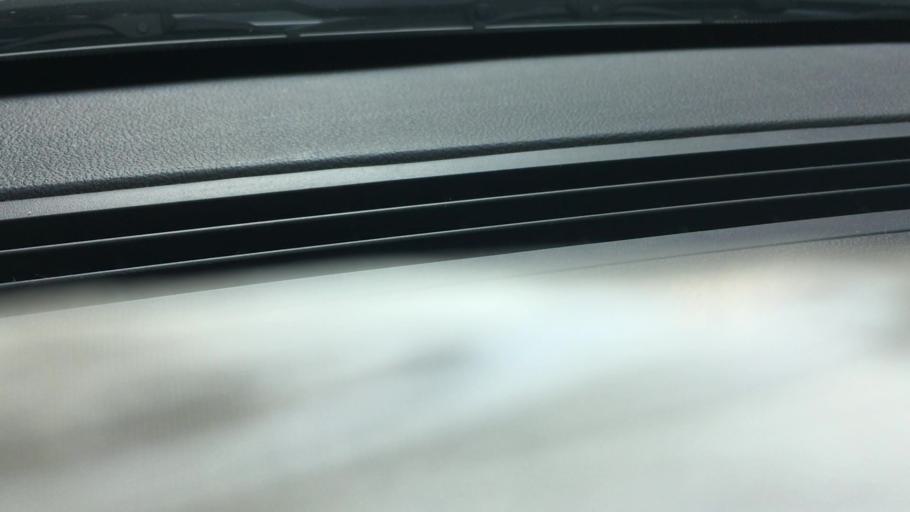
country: US
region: Alabama
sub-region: Shelby County
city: Helena
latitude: 33.2478
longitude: -86.9520
